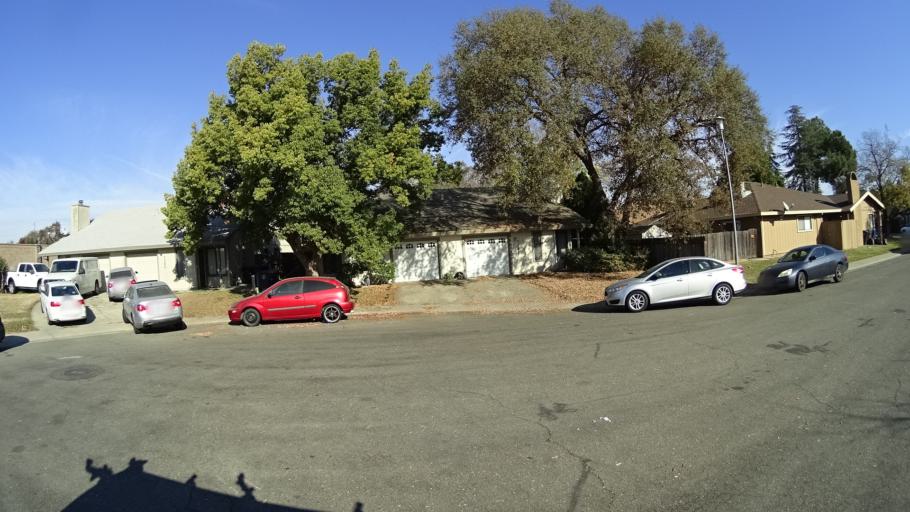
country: US
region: California
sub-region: Sacramento County
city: Citrus Heights
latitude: 38.6919
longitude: -121.2946
